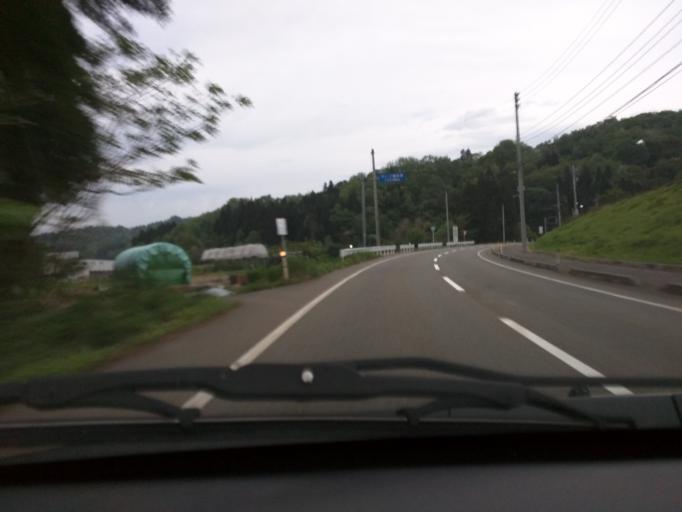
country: JP
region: Niigata
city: Ojiya
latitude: 37.3087
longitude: 138.7706
